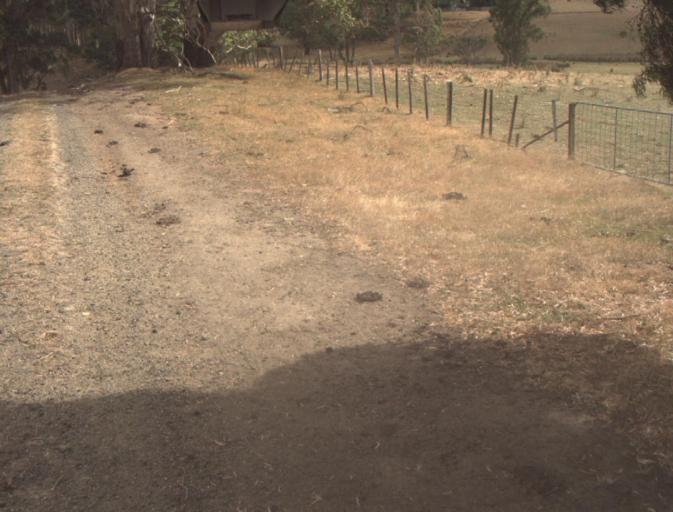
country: AU
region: Tasmania
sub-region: Dorset
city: Scottsdale
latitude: -41.4520
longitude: 147.6012
